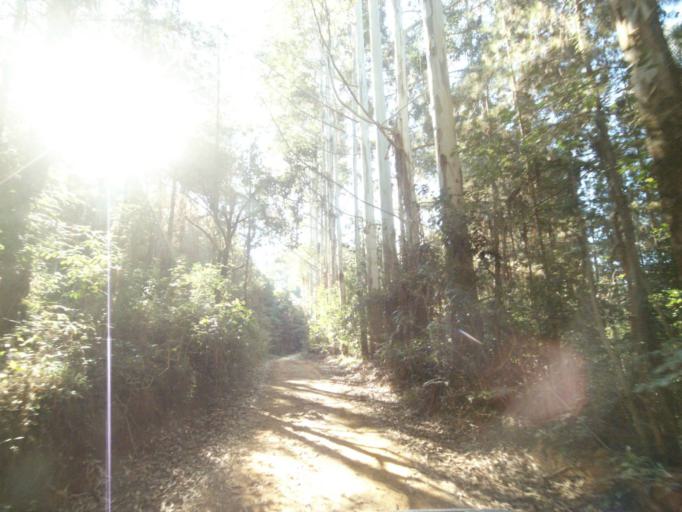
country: BR
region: Parana
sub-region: Tibagi
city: Tibagi
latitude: -24.5548
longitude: -50.4723
